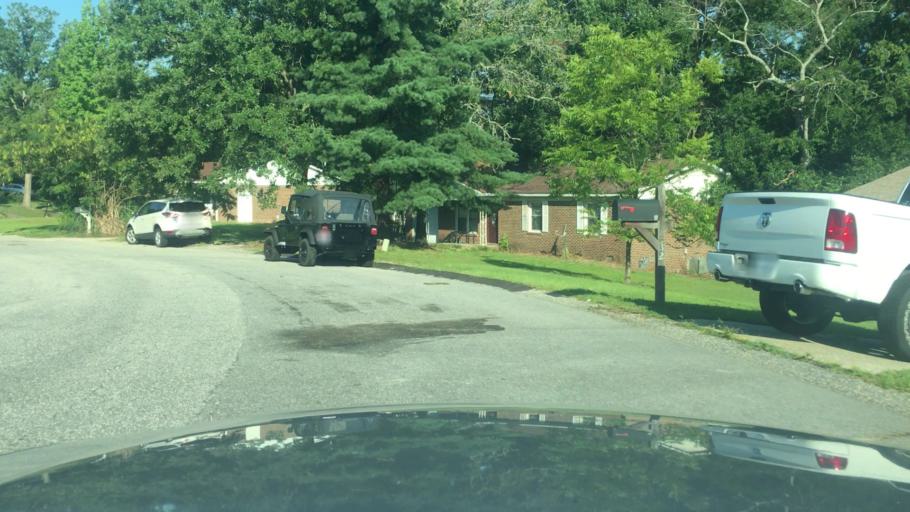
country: US
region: North Carolina
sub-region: Cumberland County
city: Spring Lake
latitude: 35.1598
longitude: -78.9071
